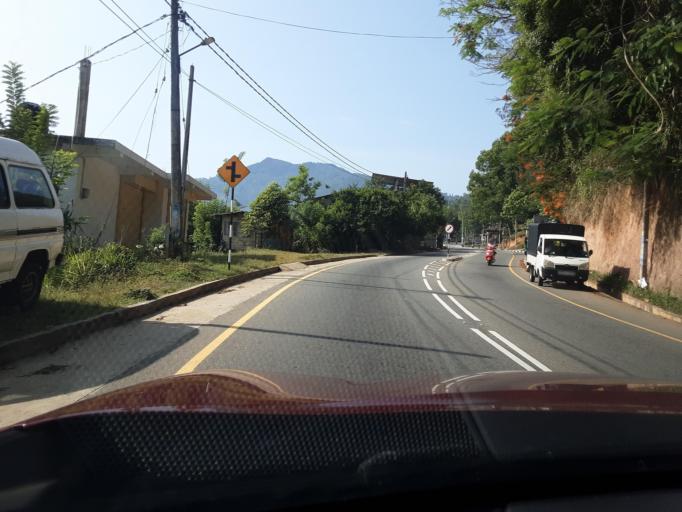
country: LK
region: Uva
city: Badulla
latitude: 6.9849
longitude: 81.0788
